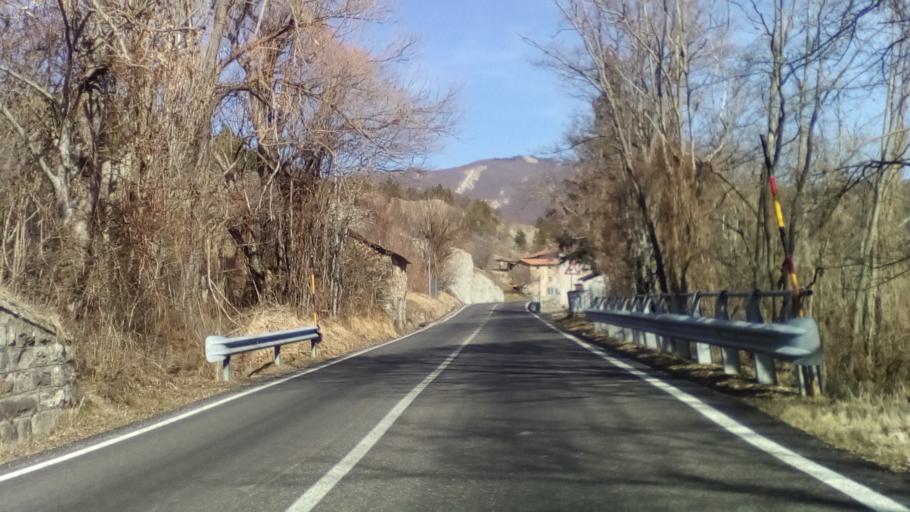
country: IT
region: Emilia-Romagna
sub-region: Provincia di Modena
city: Riolunato
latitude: 44.2453
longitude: 10.6329
